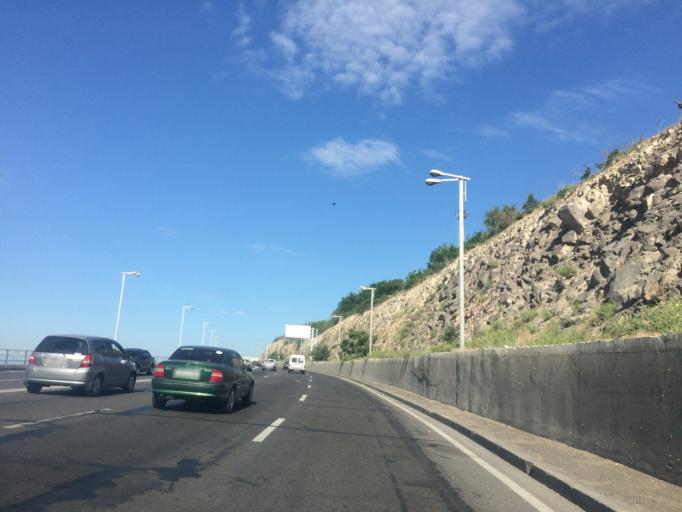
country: AM
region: Yerevan
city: Yerevan
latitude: 40.1944
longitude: 44.5266
